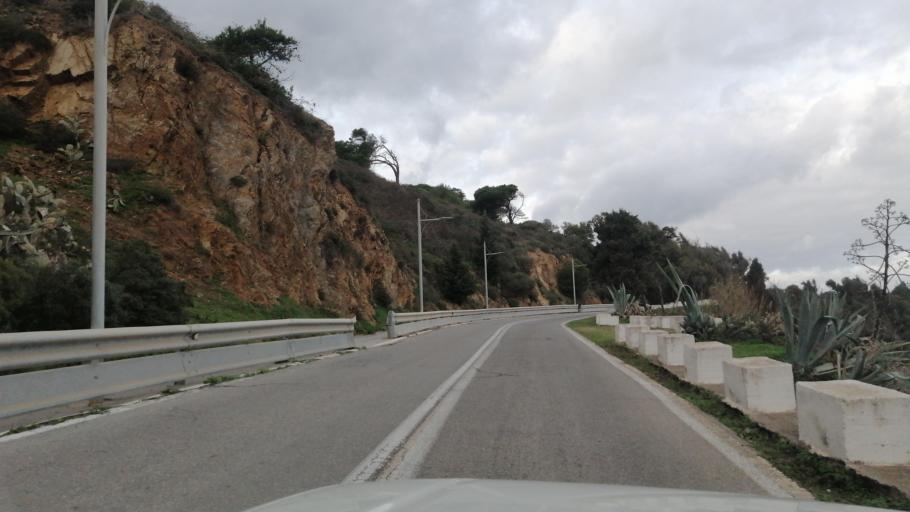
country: ES
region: Ceuta
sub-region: Ceuta
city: Ceuta
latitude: 35.8954
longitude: -5.2861
